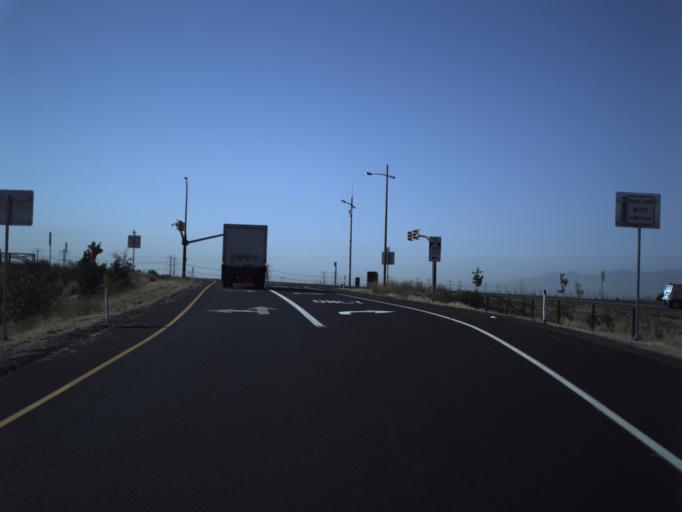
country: US
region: Utah
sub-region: Davis County
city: West Bountiful
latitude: 40.8849
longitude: -111.9382
